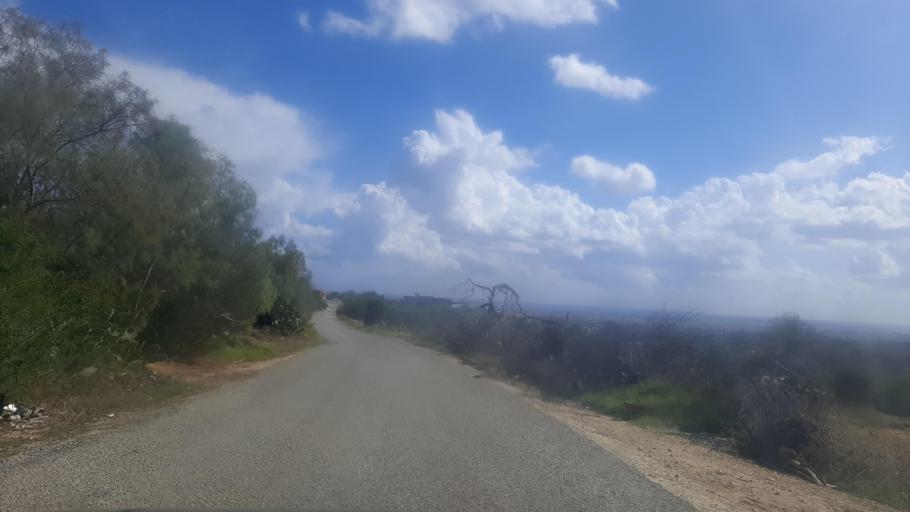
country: TN
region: Nabul
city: Dar Chabanne
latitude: 36.4992
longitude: 10.7144
